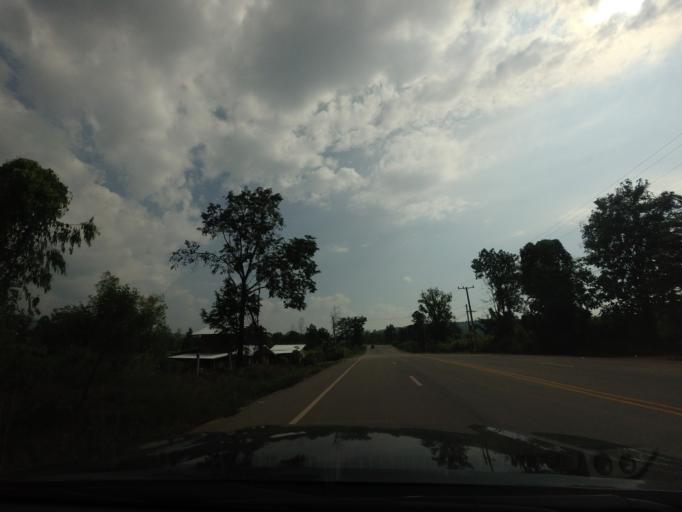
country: TH
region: Phitsanulok
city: Nakhon Thai
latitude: 17.0284
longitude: 100.9124
